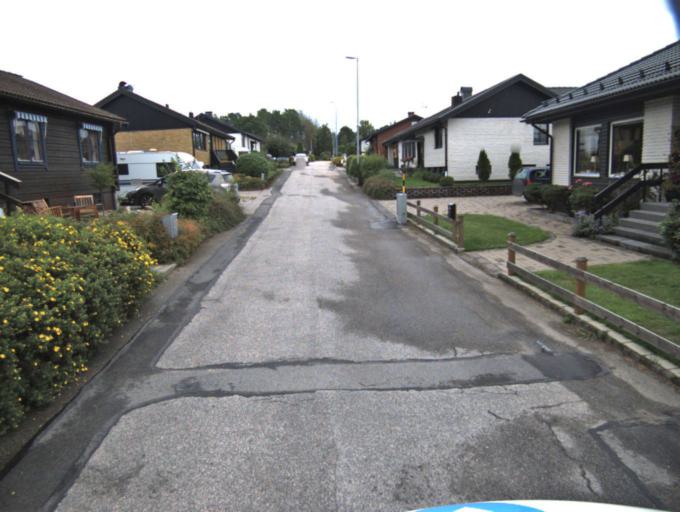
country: SE
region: Vaestra Goetaland
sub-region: Ulricehamns Kommun
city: Ulricehamn
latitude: 57.7878
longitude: 13.4283
